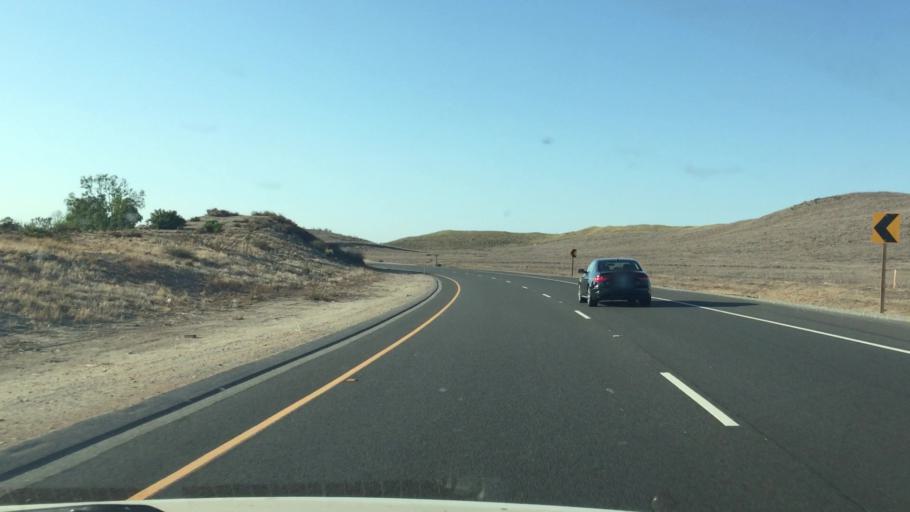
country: US
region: California
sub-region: Orange County
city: Laguna Woods
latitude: 33.6218
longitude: -117.7558
